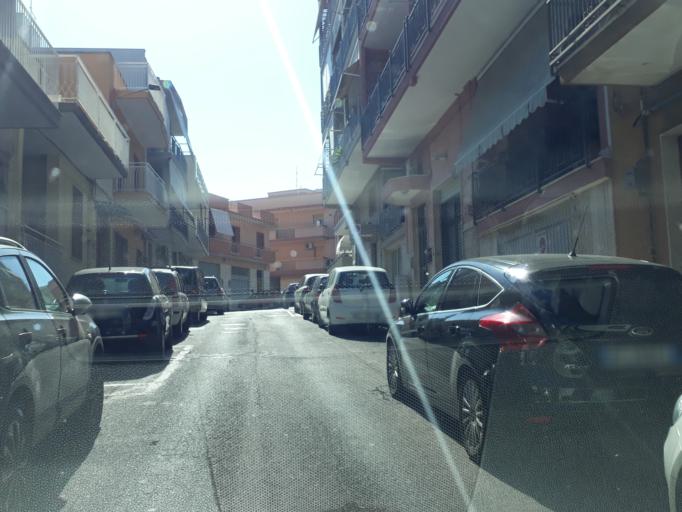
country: IT
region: Apulia
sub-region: Provincia di Bari
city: Monopoli
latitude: 40.9495
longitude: 17.2948
